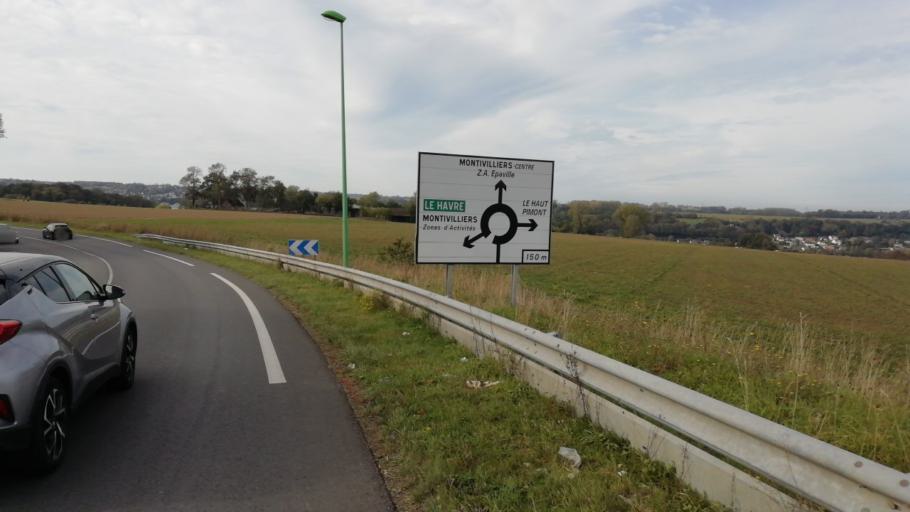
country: FR
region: Haute-Normandie
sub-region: Departement de la Seine-Maritime
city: Epouville
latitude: 49.5423
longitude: 0.2158
